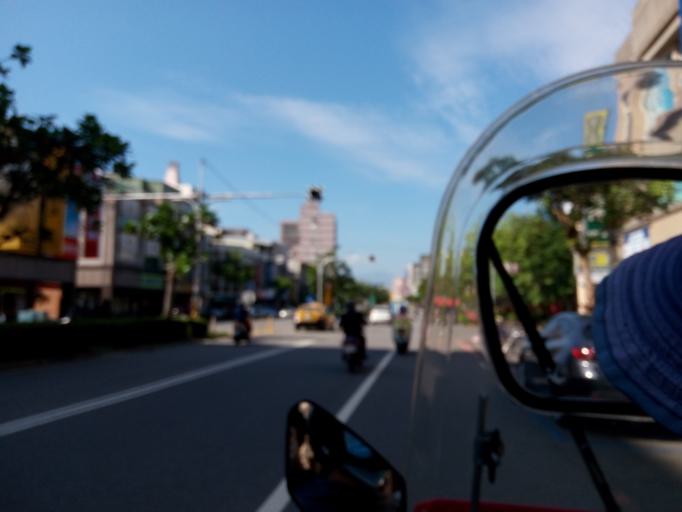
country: TW
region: Taiwan
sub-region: Yilan
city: Yilan
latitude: 24.6804
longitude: 121.7632
